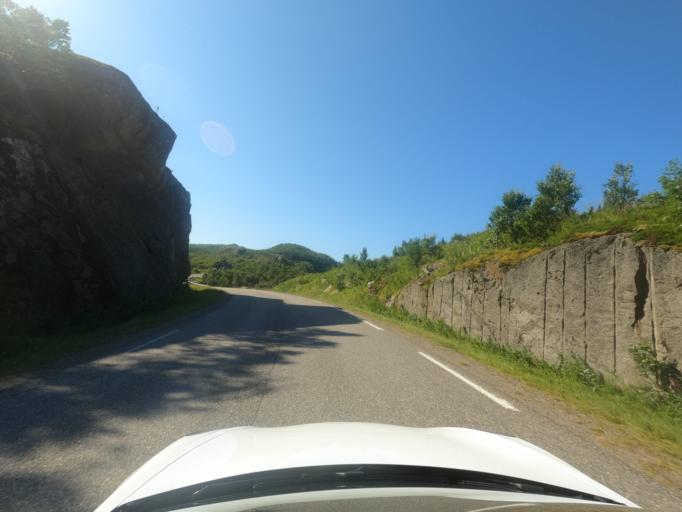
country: NO
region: Nordland
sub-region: Hadsel
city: Stokmarknes
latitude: 68.4374
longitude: 15.1833
